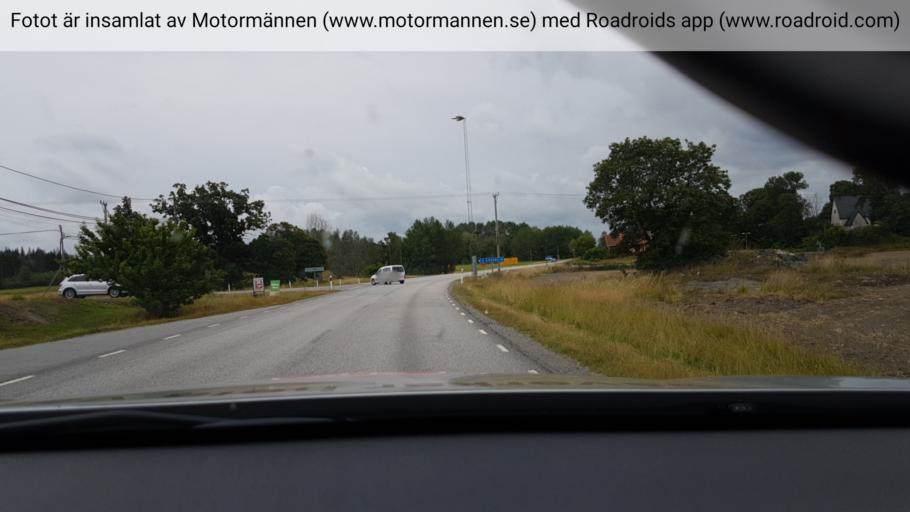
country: SE
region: Stockholm
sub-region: Vallentuna Kommun
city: Vallentuna
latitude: 59.6696
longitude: 18.0478
